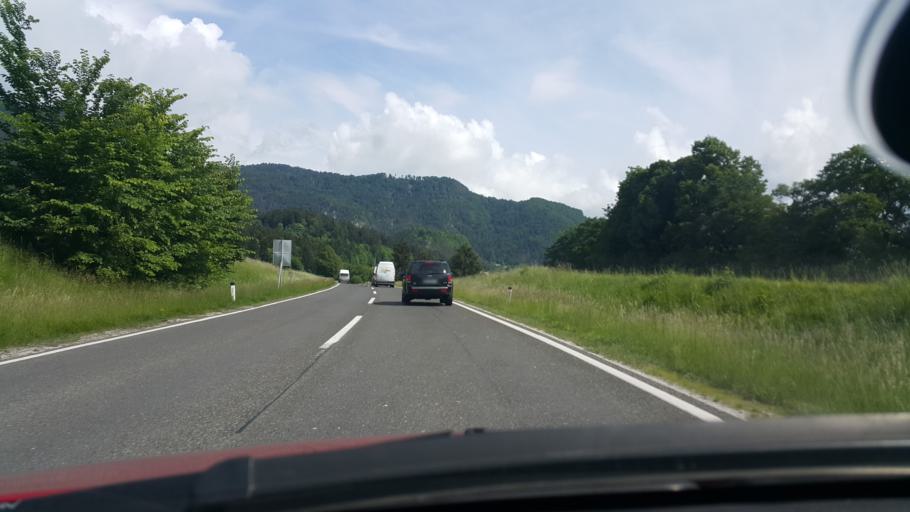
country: SI
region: Trzic
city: Bistrica pri Trzicu
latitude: 46.3422
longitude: 14.2862
